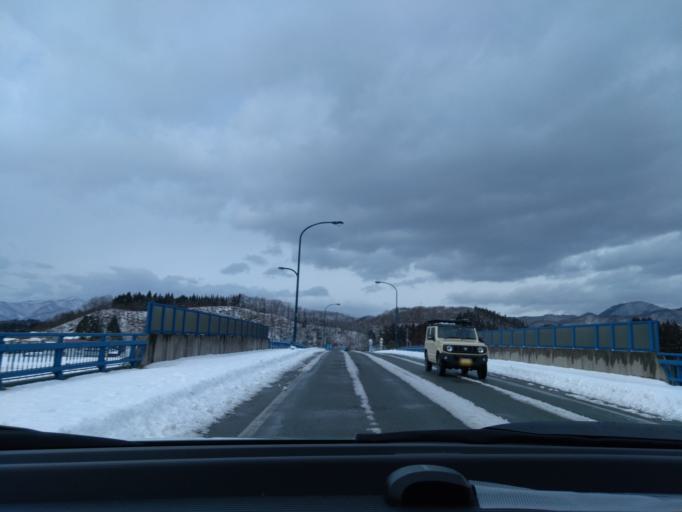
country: JP
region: Akita
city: Kakunodatemachi
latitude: 39.6233
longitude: 140.6299
